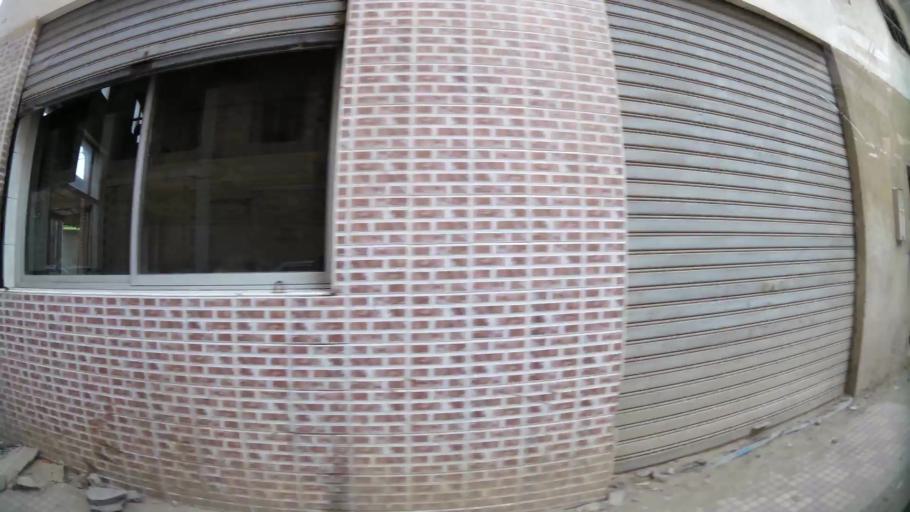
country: MA
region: Oriental
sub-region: Nador
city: Nador
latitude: 35.1675
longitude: -2.9329
